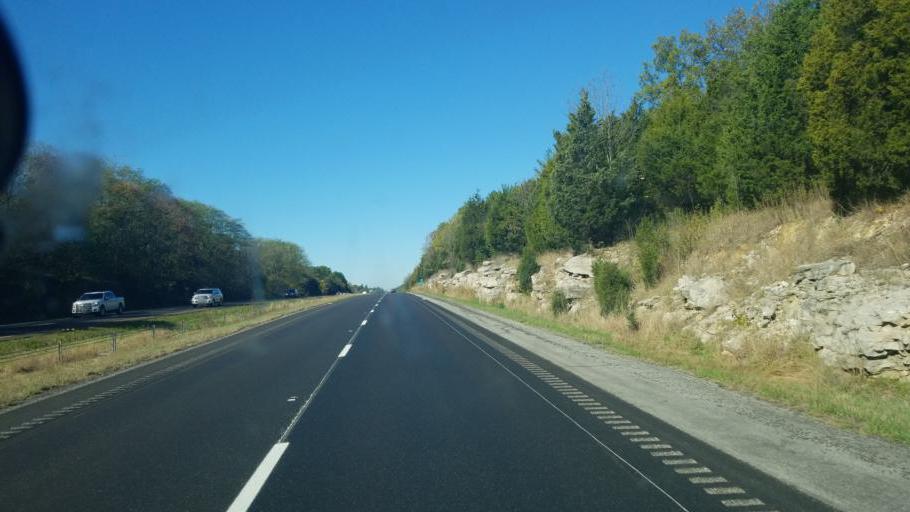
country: US
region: Missouri
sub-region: Boone County
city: Columbia
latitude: 38.9727
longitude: -92.4607
